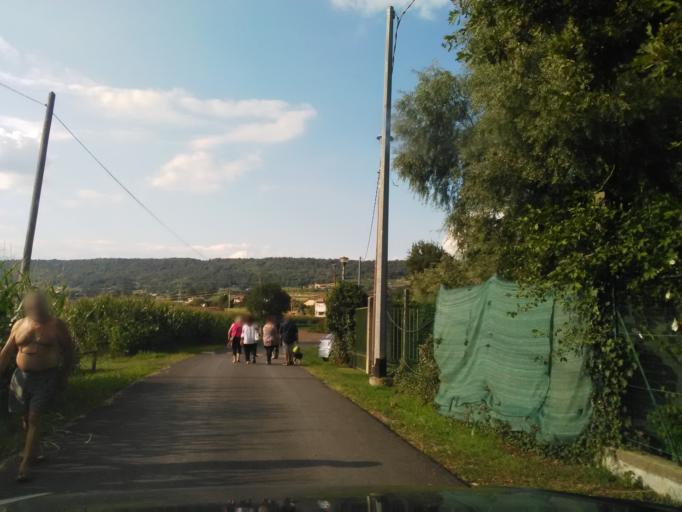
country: IT
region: Piedmont
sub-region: Provincia di Biella
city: Zimone
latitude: 45.4294
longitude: 8.0251
